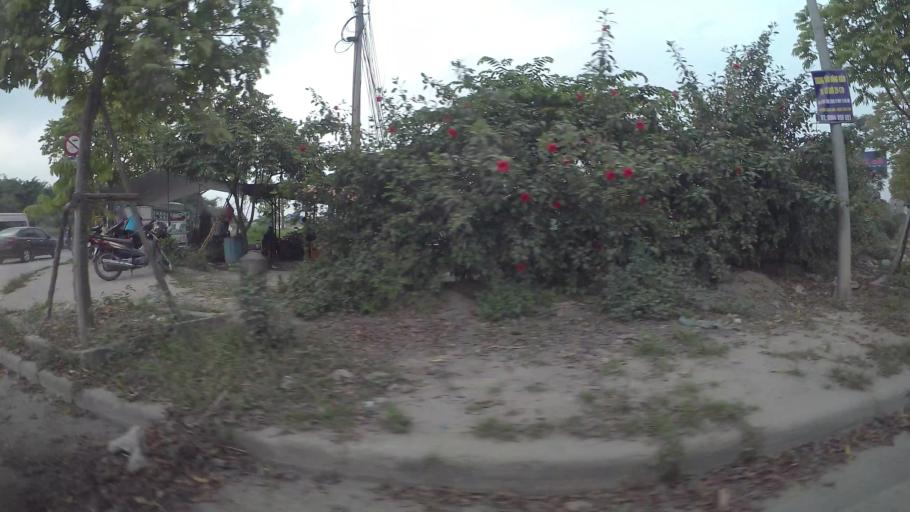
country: VN
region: Ha Noi
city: Trau Quy
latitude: 21.0030
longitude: 105.9095
